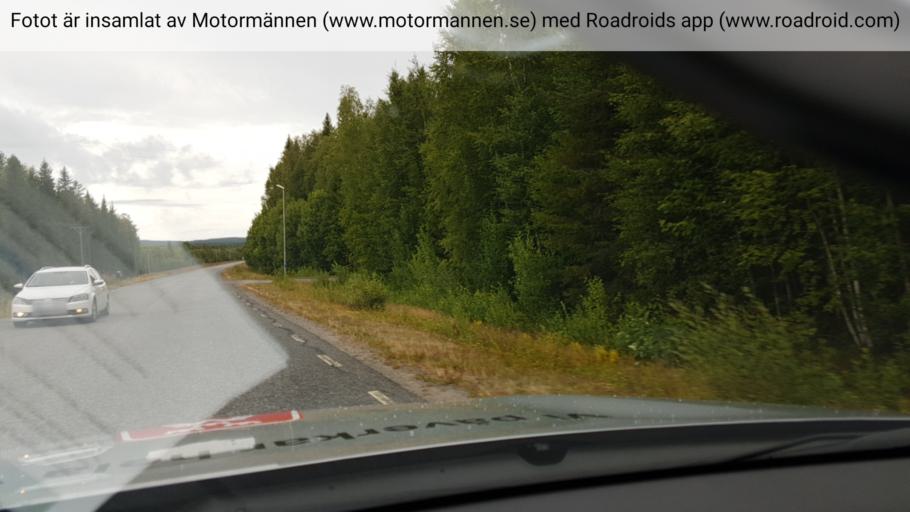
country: SE
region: Norrbotten
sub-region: Bodens Kommun
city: Boden
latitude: 65.8501
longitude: 21.4504
